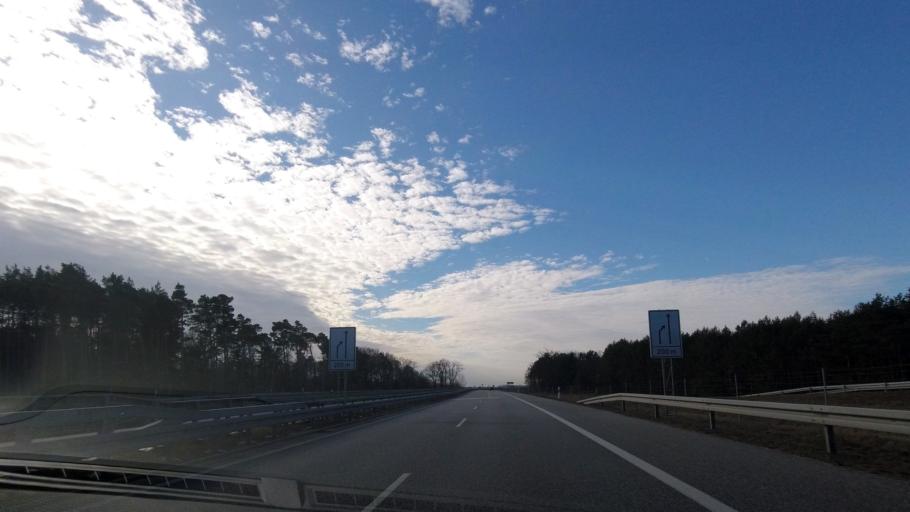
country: DE
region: Brandenburg
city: Luckenwalde
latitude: 52.1298
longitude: 13.2168
